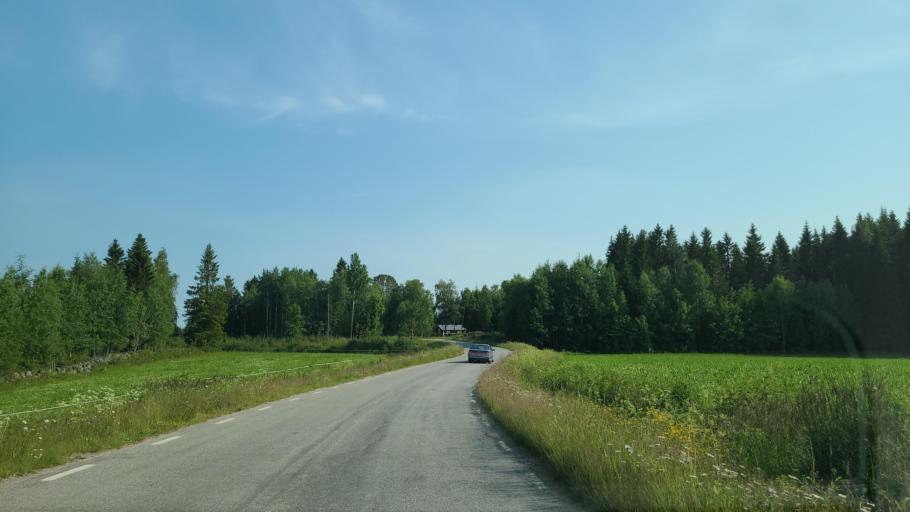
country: SE
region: Vaesterbotten
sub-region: Skelleftea Kommun
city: Burea
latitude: 64.3467
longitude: 21.3397
